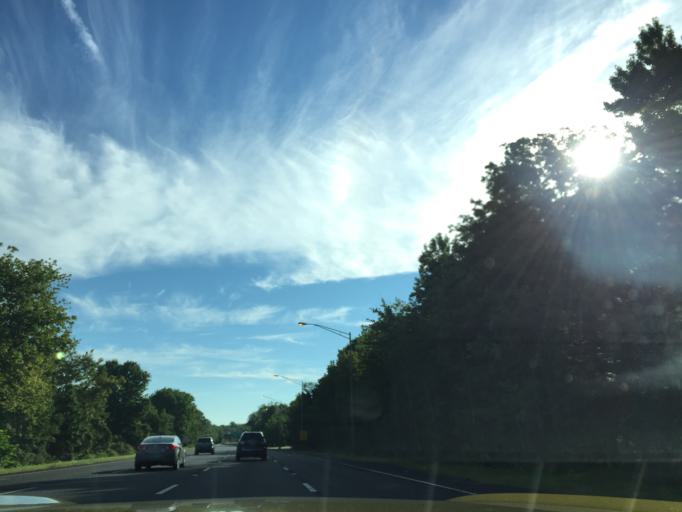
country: US
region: New Jersey
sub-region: Somerset County
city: Watchung
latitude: 40.6576
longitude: -74.4399
